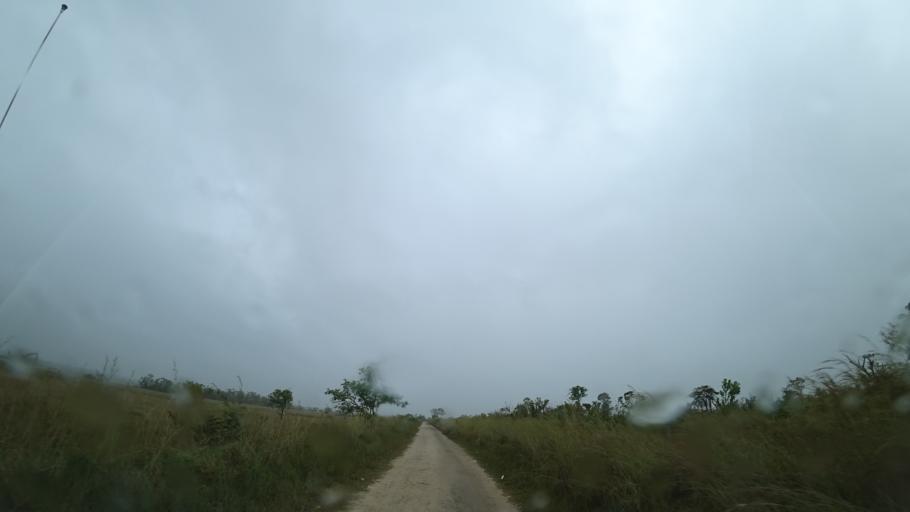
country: MZ
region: Sofala
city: Dondo
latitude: -19.5774
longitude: 35.1131
